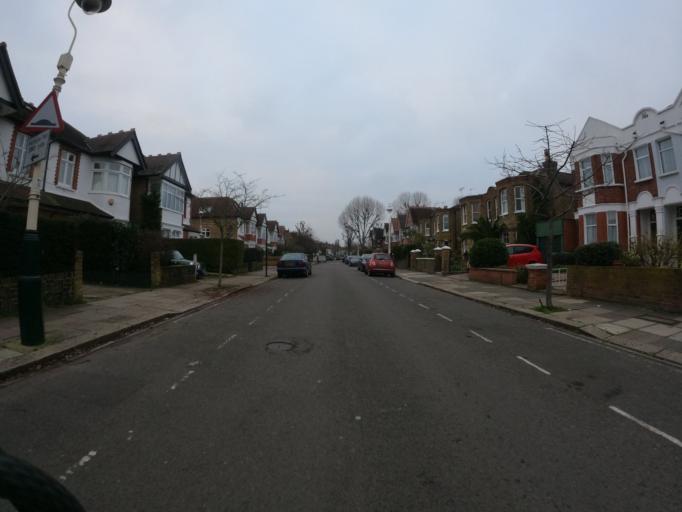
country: GB
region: England
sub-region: Greater London
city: Ealing
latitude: 51.5057
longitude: -0.3137
